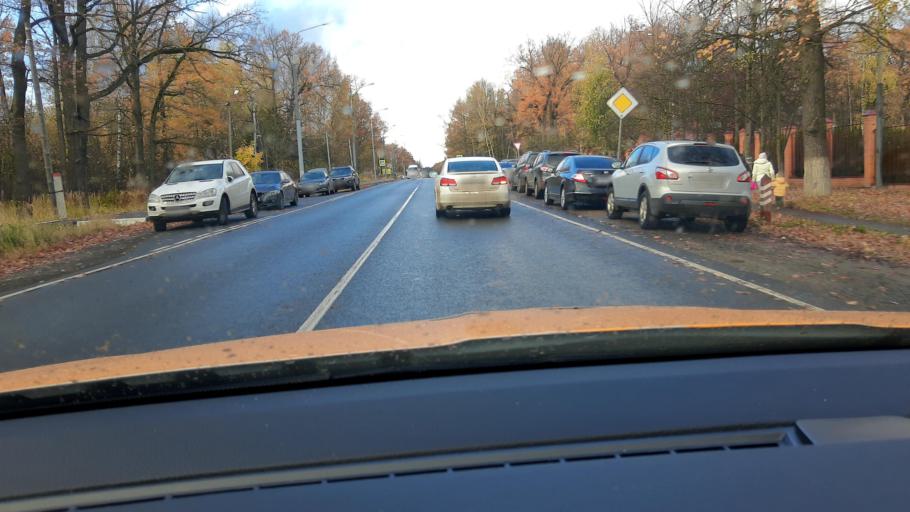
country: RU
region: Moskovskaya
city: Odintsovo
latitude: 55.6815
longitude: 37.2757
